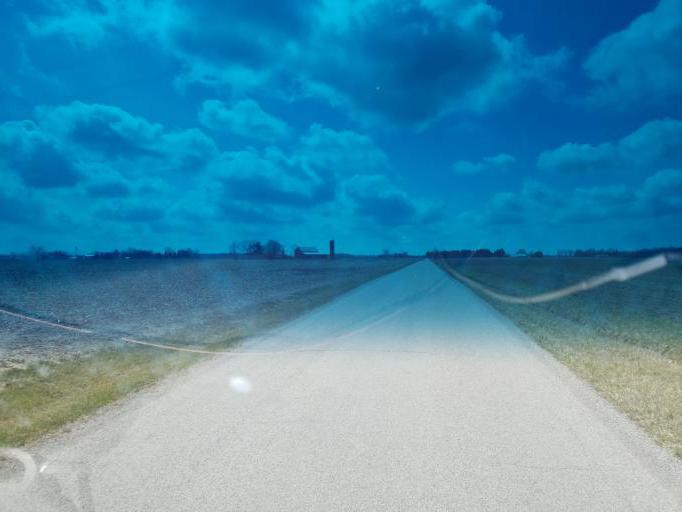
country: US
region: Ohio
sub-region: Crawford County
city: Bucyrus
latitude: 40.7859
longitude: -83.0267
